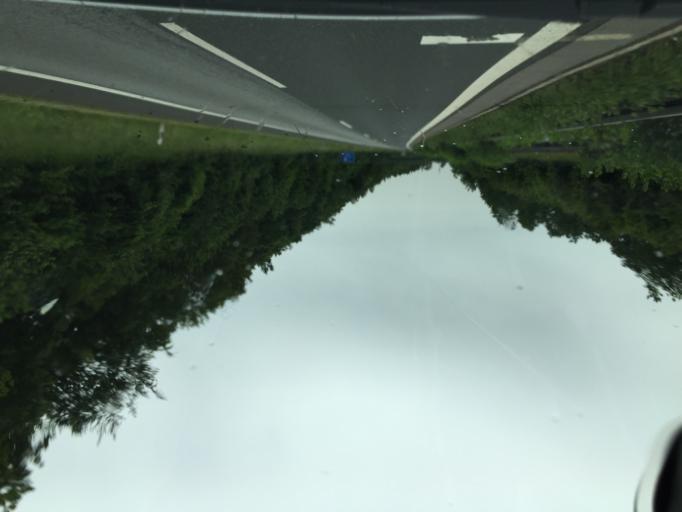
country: DE
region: Bavaria
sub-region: Regierungsbezirk Unterfranken
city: Donnersdorf
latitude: 50.0036
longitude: 10.3991
